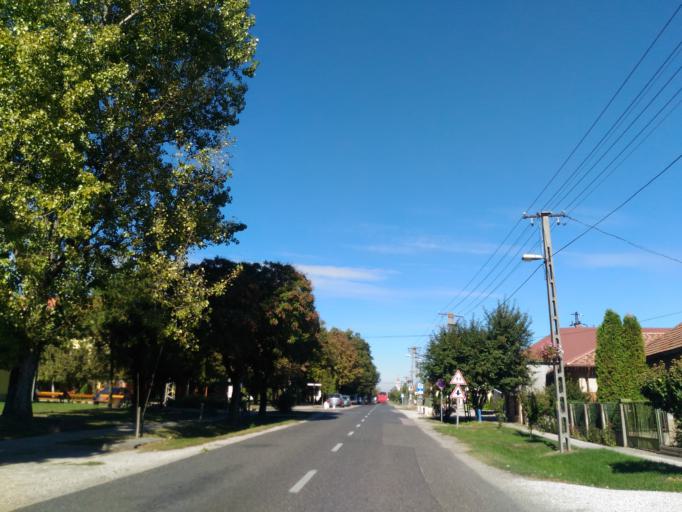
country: HU
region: Fejer
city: Ivancsa
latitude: 47.1500
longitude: 18.8281
